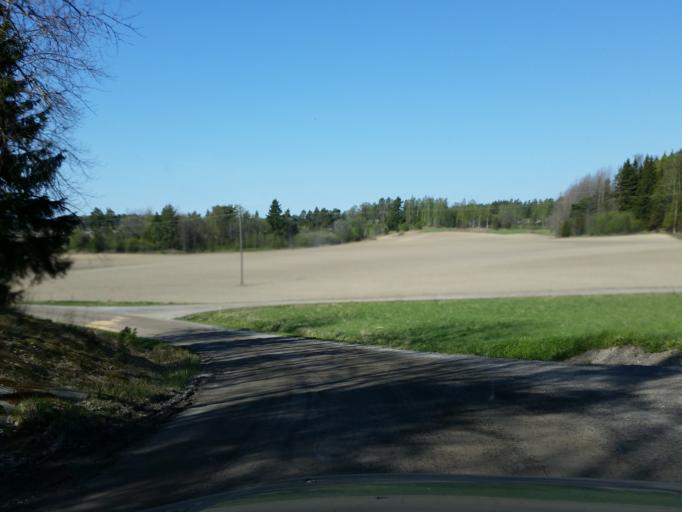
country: FI
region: Uusimaa
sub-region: Raaseporin
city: Karis
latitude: 60.1420
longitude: 23.7211
